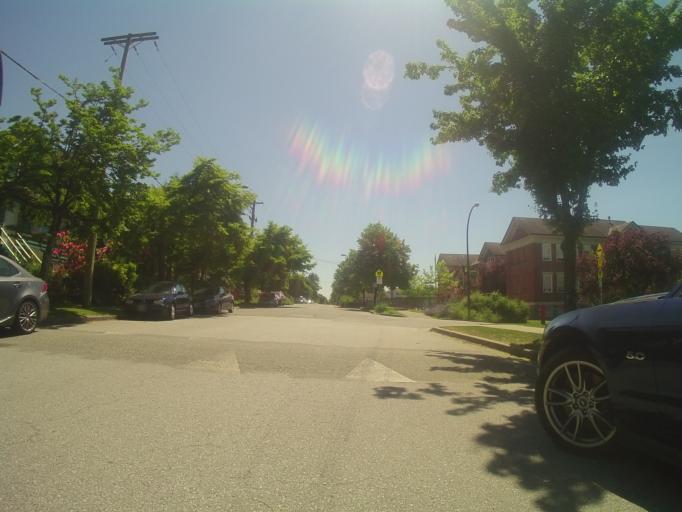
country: CA
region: British Columbia
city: Vancouver
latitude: 49.2480
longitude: -123.1051
